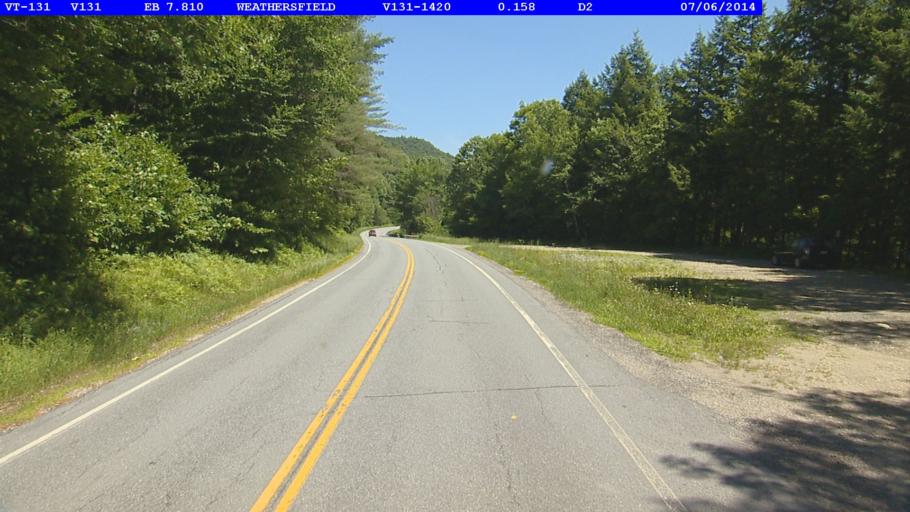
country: US
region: Vermont
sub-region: Windsor County
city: Springfield
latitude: 43.3947
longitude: -72.5352
